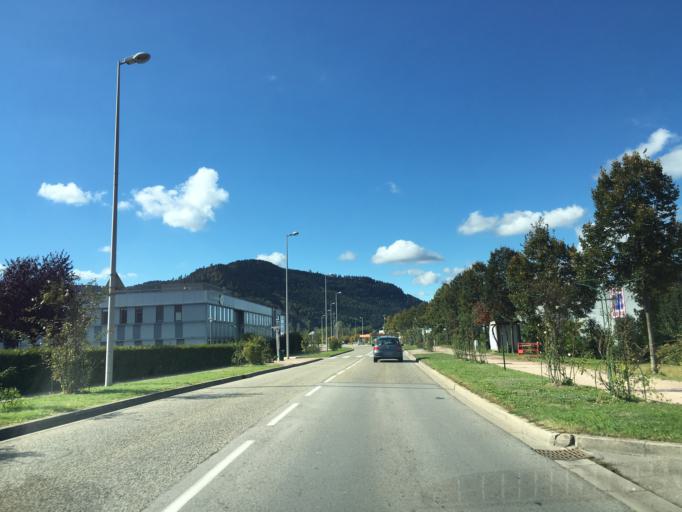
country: FR
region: Lorraine
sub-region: Departement des Vosges
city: Saint-Die-des-Vosges
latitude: 48.2921
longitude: 6.9378
